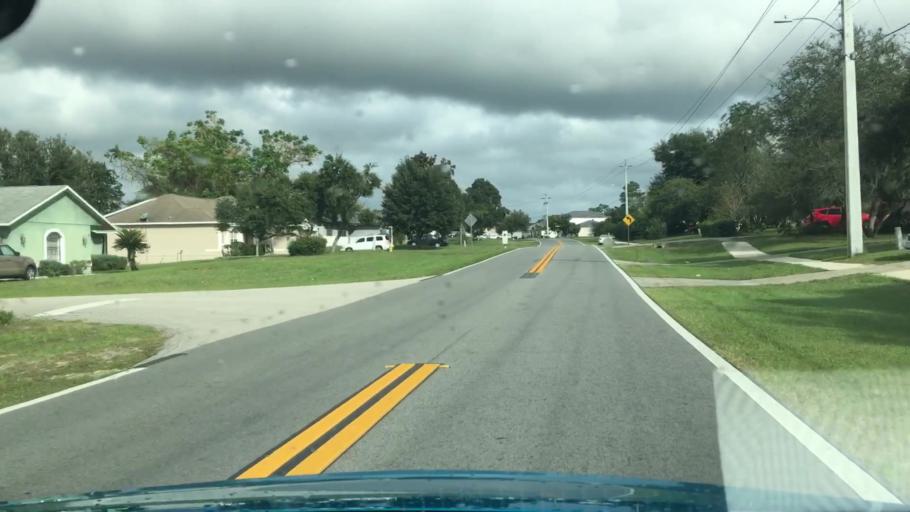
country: US
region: Florida
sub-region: Volusia County
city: Lake Helen
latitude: 28.9539
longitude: -81.1859
